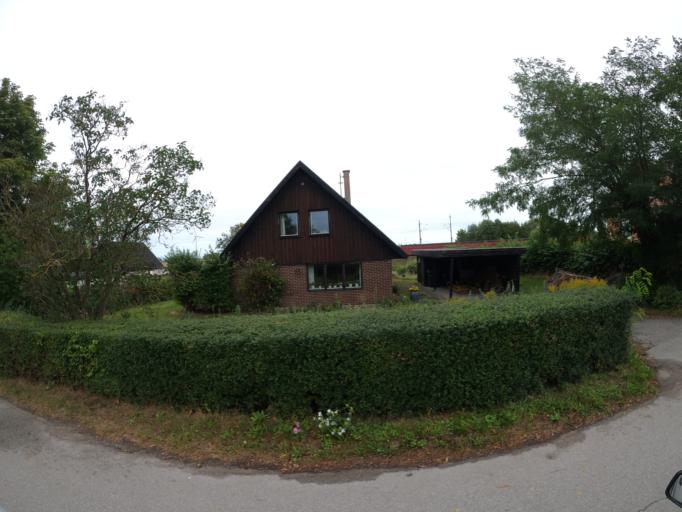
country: SE
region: Skane
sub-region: Kavlinge Kommun
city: Kaevlinge
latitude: 55.7457
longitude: 13.1473
